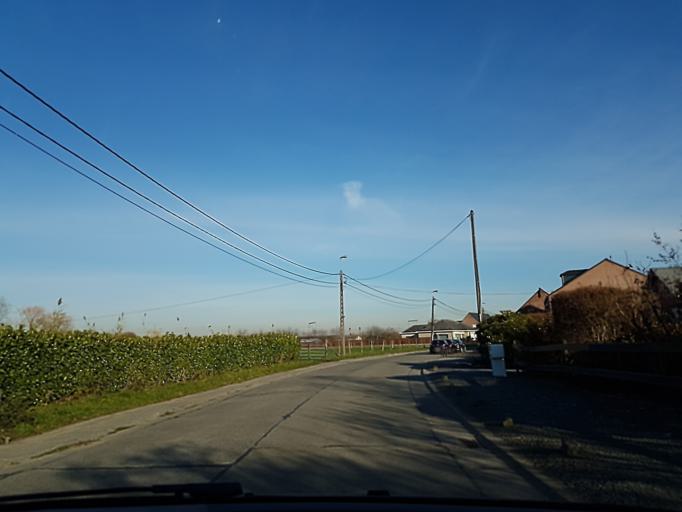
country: BE
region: Flanders
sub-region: Provincie Vlaams-Brabant
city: Kapelle-op-den-Bos
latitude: 51.0091
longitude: 4.3843
